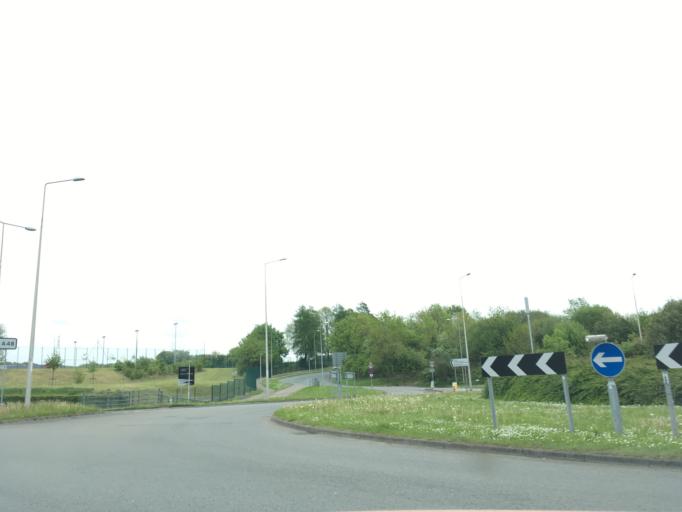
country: GB
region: Wales
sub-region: Newport
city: Llanwern
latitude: 51.5866
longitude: -2.9385
